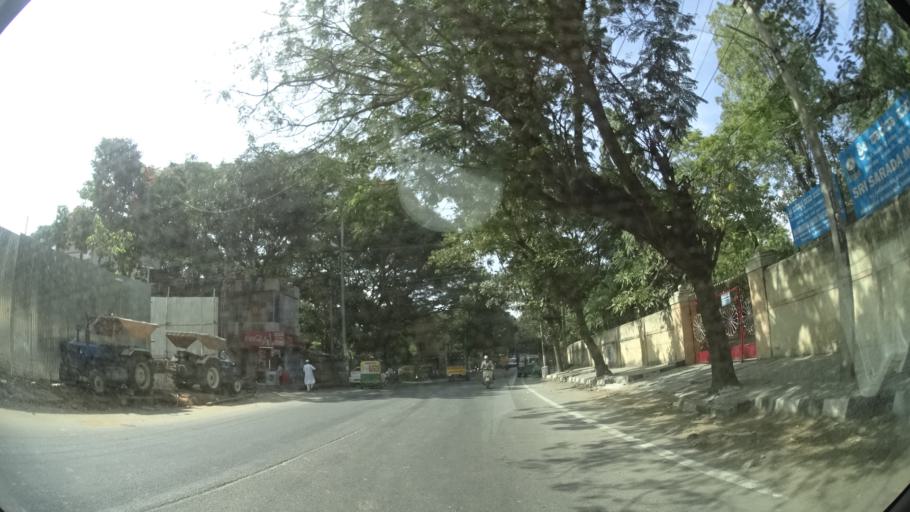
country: IN
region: Karnataka
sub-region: Bangalore Urban
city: Bangalore
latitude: 13.0032
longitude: 77.5966
